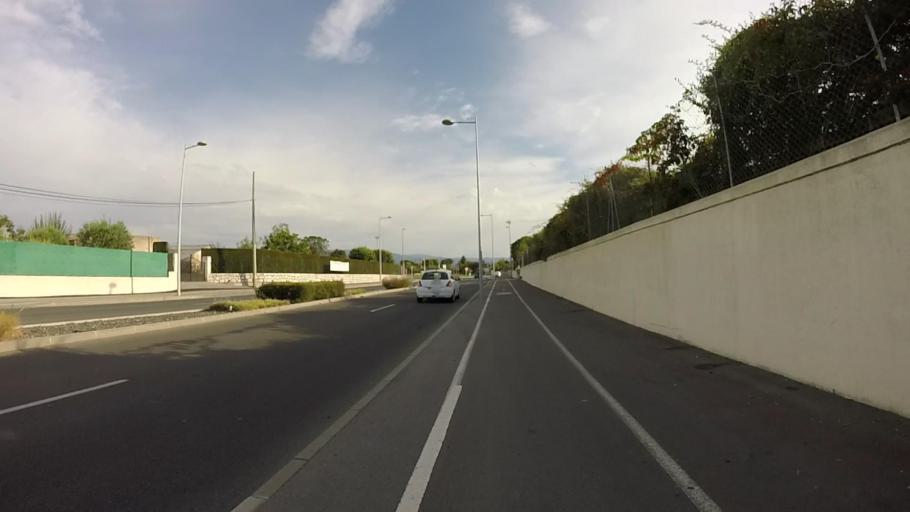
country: FR
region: Provence-Alpes-Cote d'Azur
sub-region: Departement des Alpes-Maritimes
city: Biot
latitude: 43.6020
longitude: 7.1127
